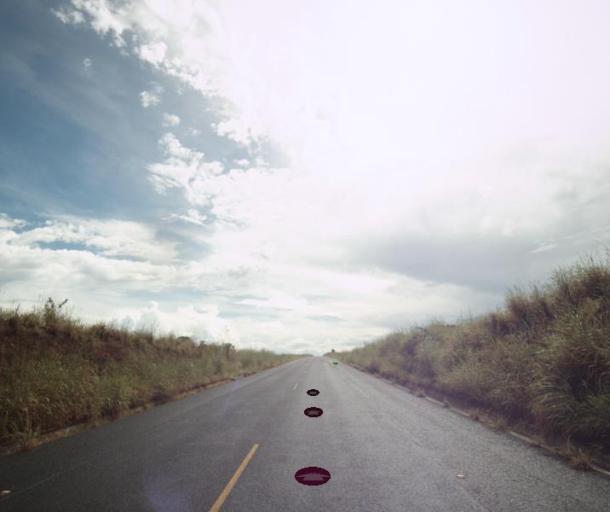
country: BR
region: Goias
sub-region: Sao Miguel Do Araguaia
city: Sao Miguel do Araguaia
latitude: -13.2965
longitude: -50.3489
